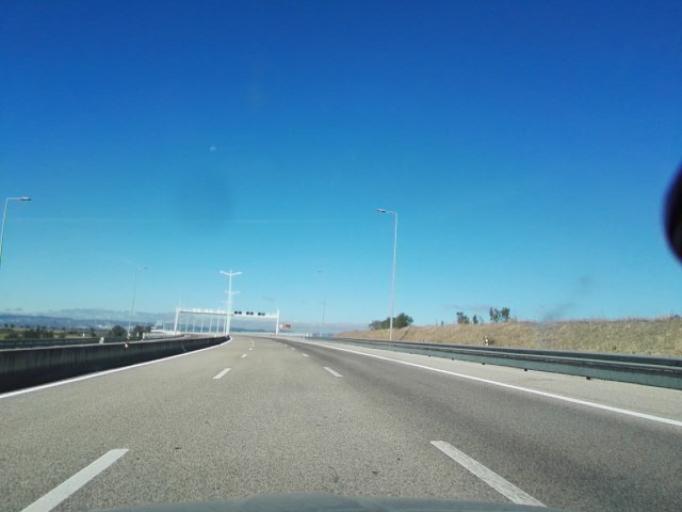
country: PT
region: Santarem
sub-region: Benavente
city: Benavente
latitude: 38.9664
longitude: -8.8437
